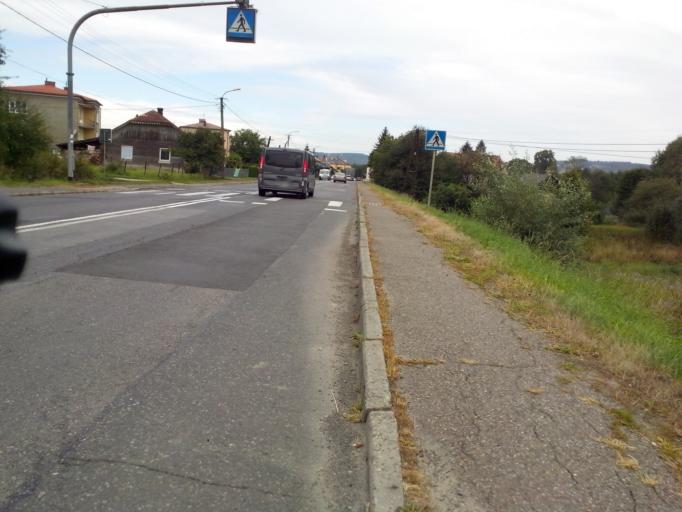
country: PL
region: Subcarpathian Voivodeship
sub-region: Powiat brzozowski
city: Domaradz
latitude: 49.7854
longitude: 21.9471
